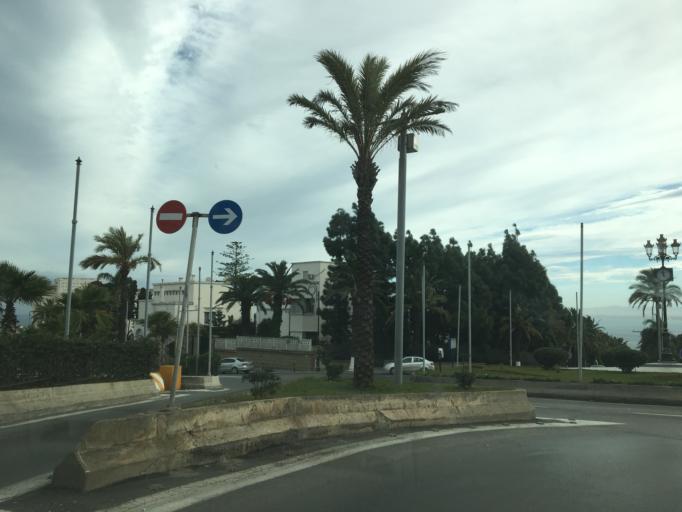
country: DZ
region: Alger
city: Algiers
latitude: 36.7788
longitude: 3.0497
